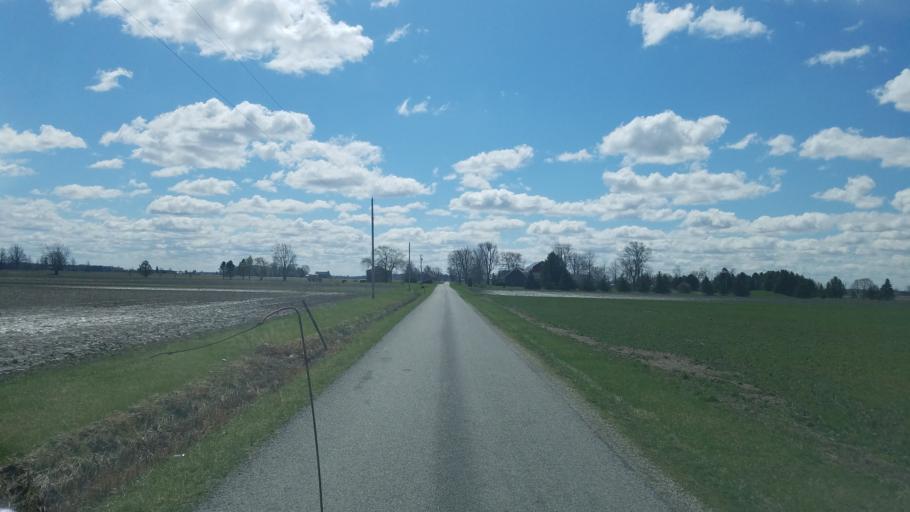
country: US
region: Ohio
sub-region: Hancock County
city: Findlay
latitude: 41.0204
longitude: -83.5109
